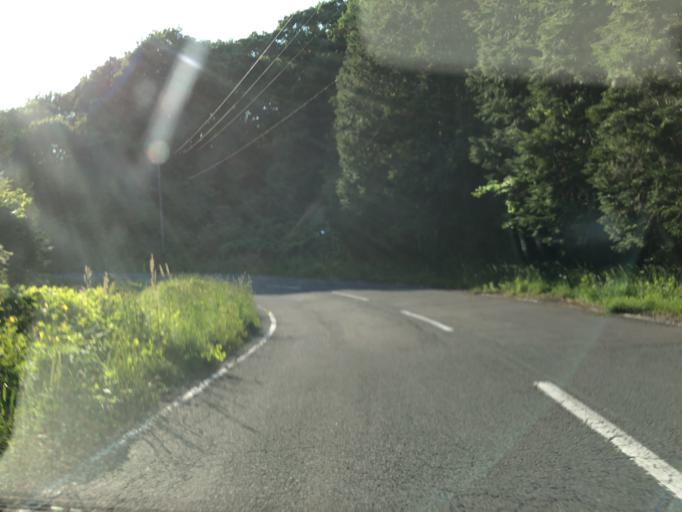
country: JP
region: Ibaraki
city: Daigo
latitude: 36.9279
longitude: 140.4516
